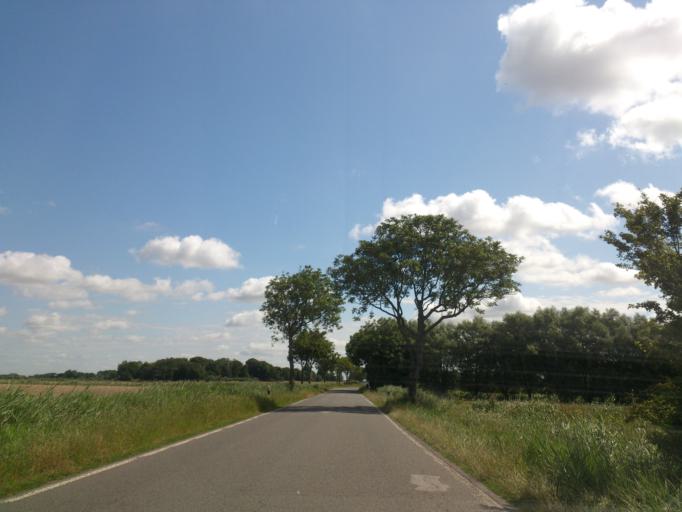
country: DE
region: Schleswig-Holstein
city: Katharinenheerd
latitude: 54.3155
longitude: 8.8596
